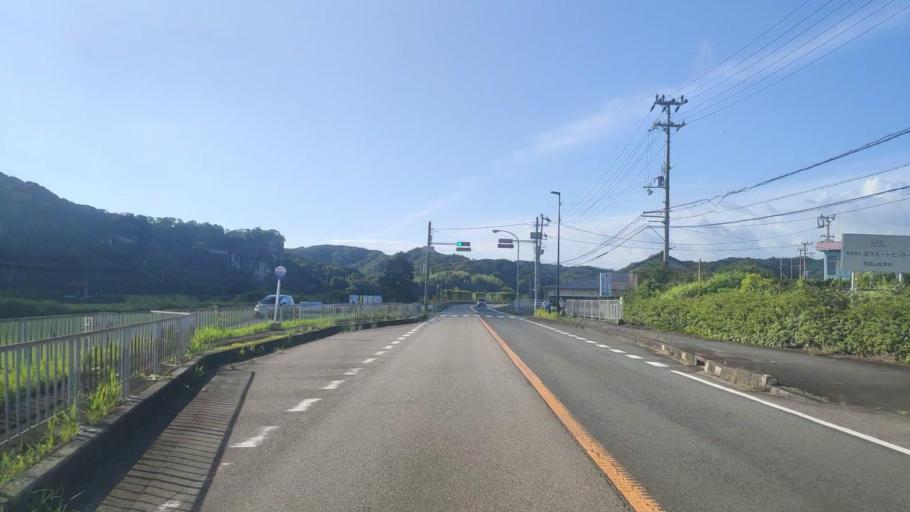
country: JP
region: Wakayama
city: Tanabe
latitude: 33.6609
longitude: 135.3992
